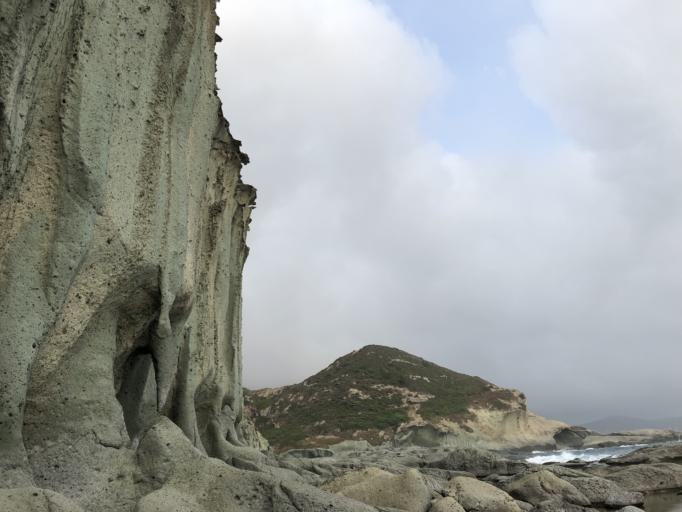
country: IT
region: Sardinia
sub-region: Provincia di Oristano
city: Bosa
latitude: 40.2987
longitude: 8.4676
